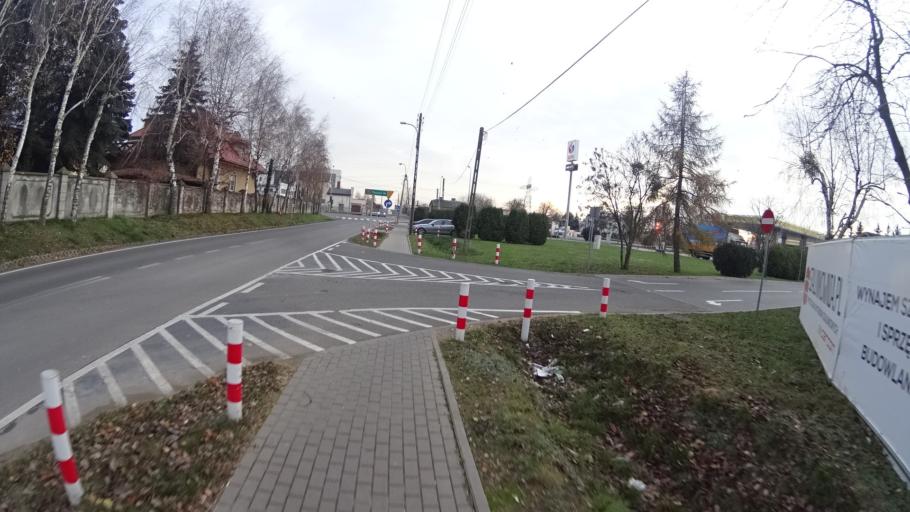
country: PL
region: Masovian Voivodeship
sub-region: Warszawa
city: Ursus
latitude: 52.2167
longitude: 20.8597
